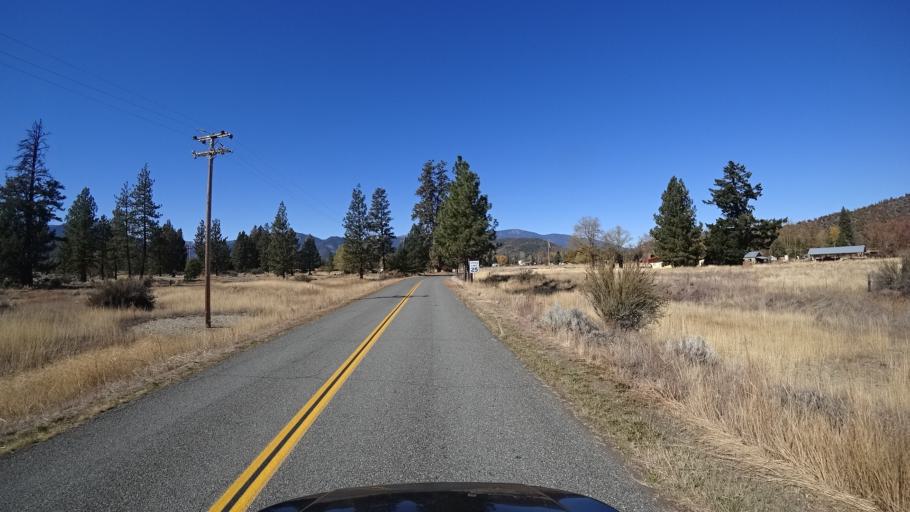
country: US
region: California
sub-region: Siskiyou County
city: Yreka
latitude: 41.5442
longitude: -122.9052
